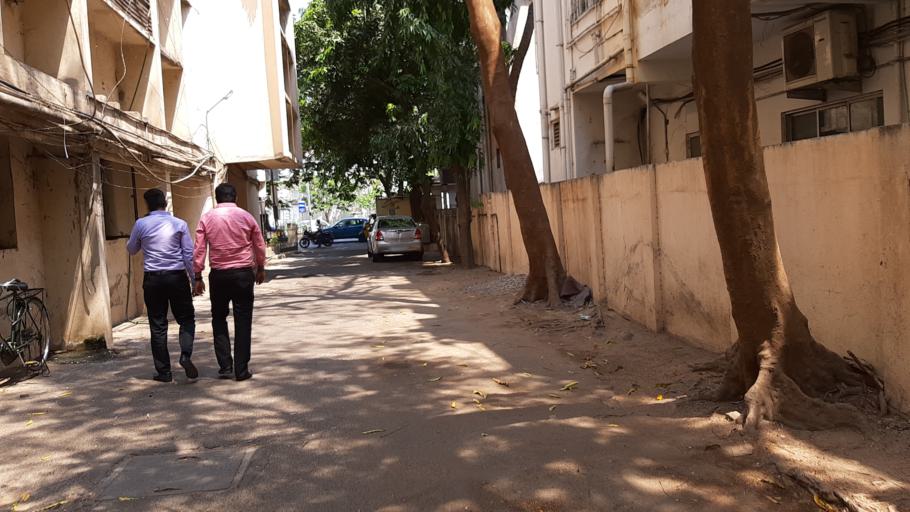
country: IN
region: Tamil Nadu
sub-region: Chennai
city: Chetput
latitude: 13.0471
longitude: 80.2426
